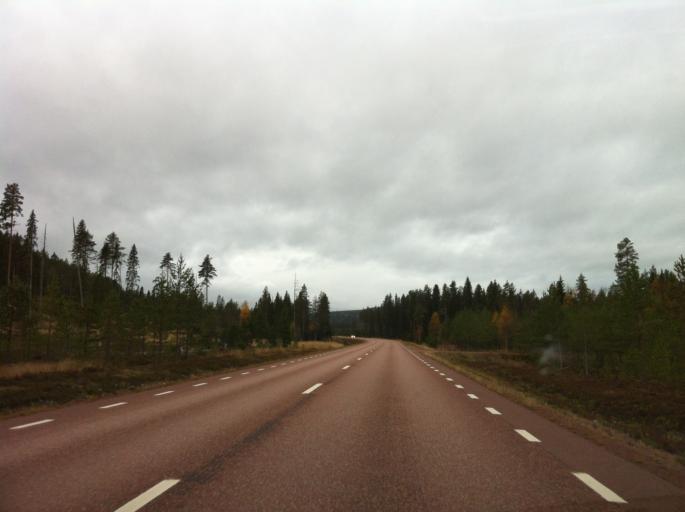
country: SE
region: Dalarna
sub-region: Alvdalens Kommun
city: AElvdalen
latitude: 61.2768
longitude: 13.8902
